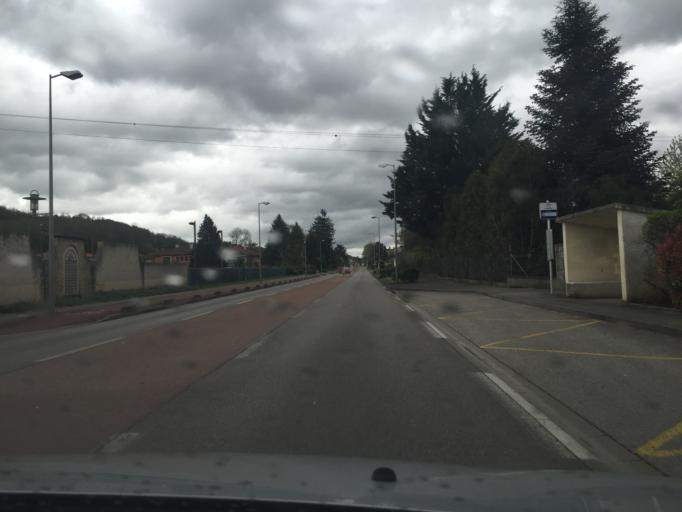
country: FR
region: Rhone-Alpes
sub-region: Departement de l'Ain
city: La Boisse
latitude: 45.8414
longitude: 5.0228
